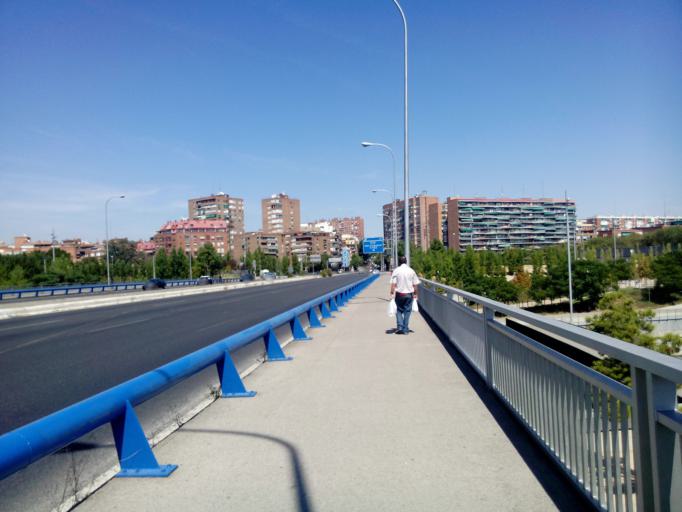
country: ES
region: Madrid
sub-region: Provincia de Madrid
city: Usera
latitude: 40.3946
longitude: -3.7048
